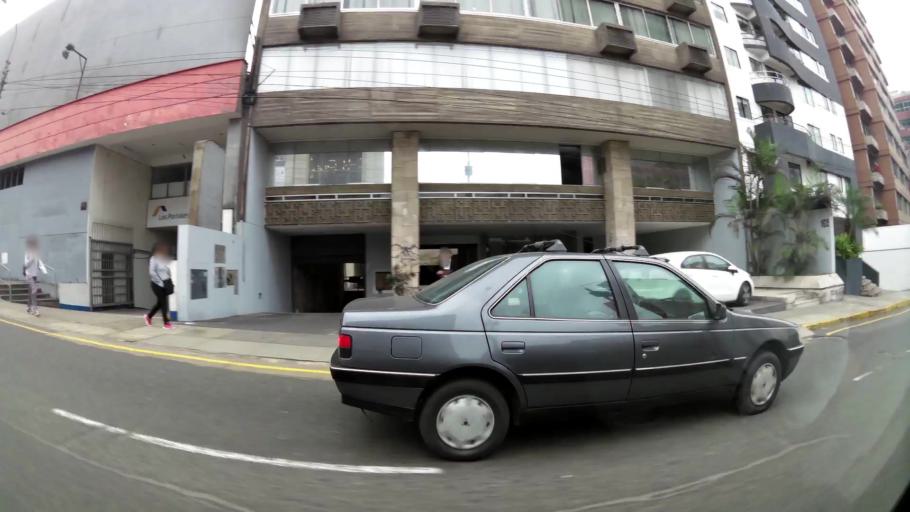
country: PE
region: Lima
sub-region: Lima
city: San Isidro
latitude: -12.1233
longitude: -77.0321
